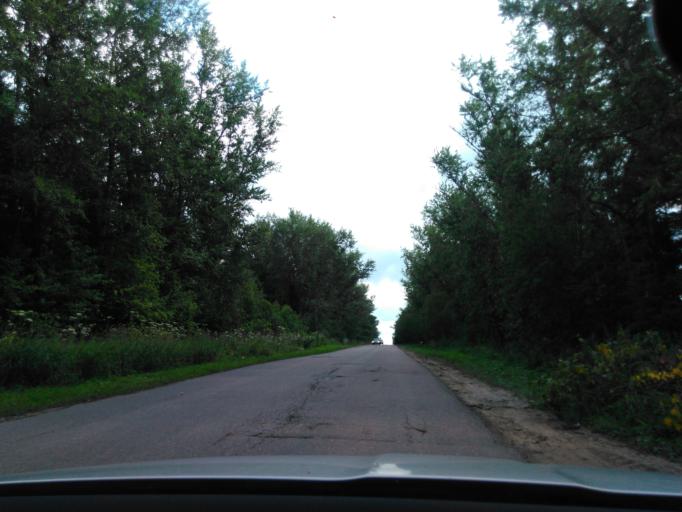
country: RU
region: Moskovskaya
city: Radumlya
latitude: 56.1217
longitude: 37.2087
